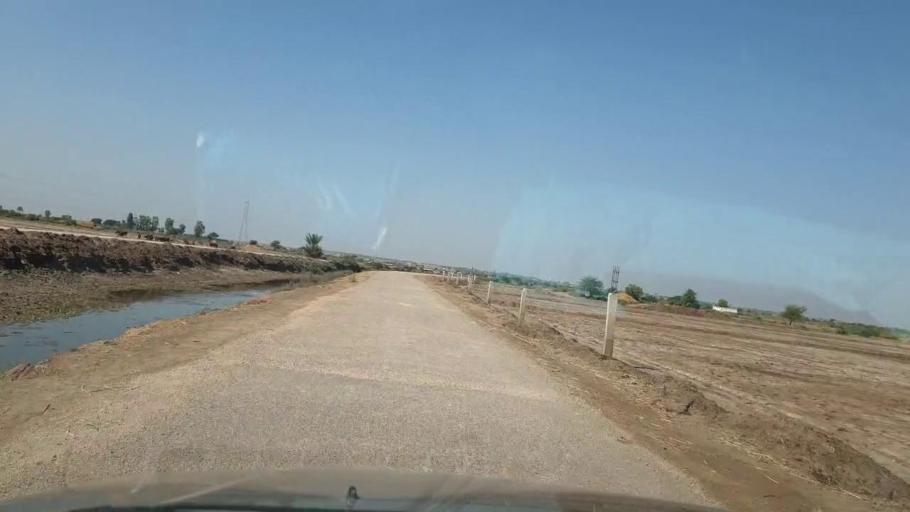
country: PK
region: Sindh
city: Thatta
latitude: 24.7230
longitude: 67.9304
